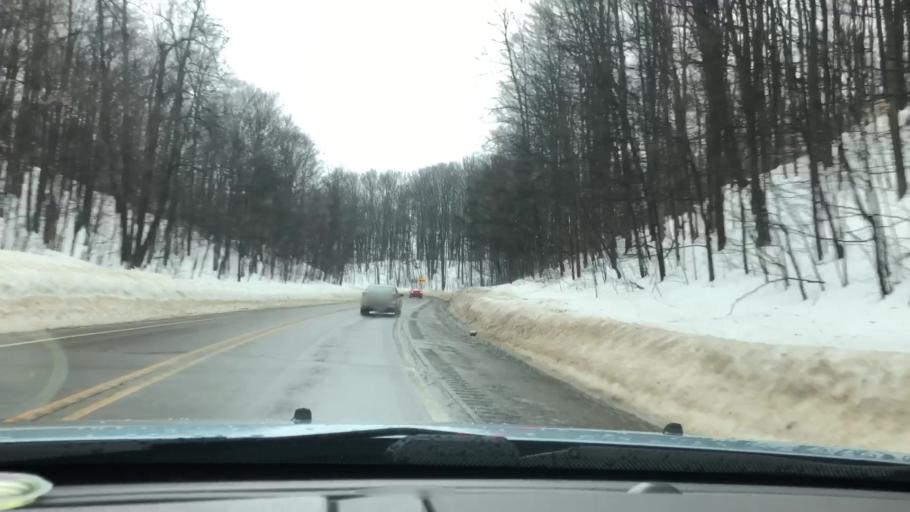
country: US
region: Michigan
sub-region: Charlevoix County
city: Boyne City
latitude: 45.0811
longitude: -84.9124
